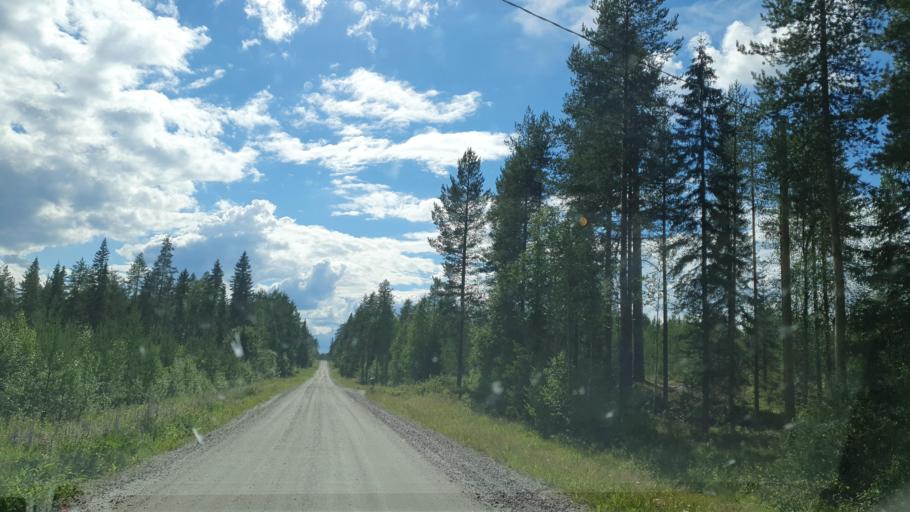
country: FI
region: Kainuu
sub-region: Kehys-Kainuu
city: Kuhmo
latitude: 64.1511
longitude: 29.7305
